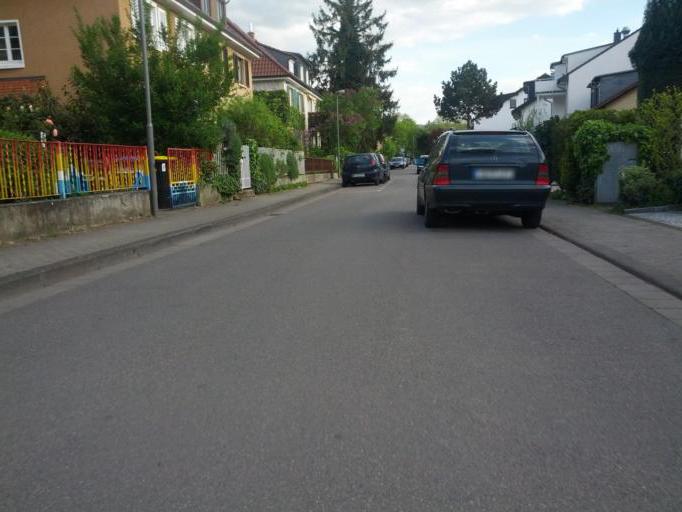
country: DE
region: Baden-Wuerttemberg
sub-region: Karlsruhe Region
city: Heidelberg
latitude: 49.4261
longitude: 8.6788
